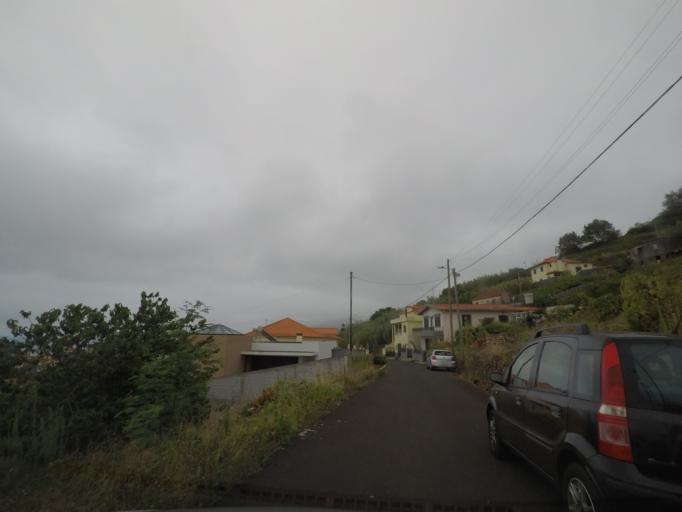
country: PT
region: Madeira
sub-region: Santana
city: Santana
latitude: 32.7681
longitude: -16.8490
